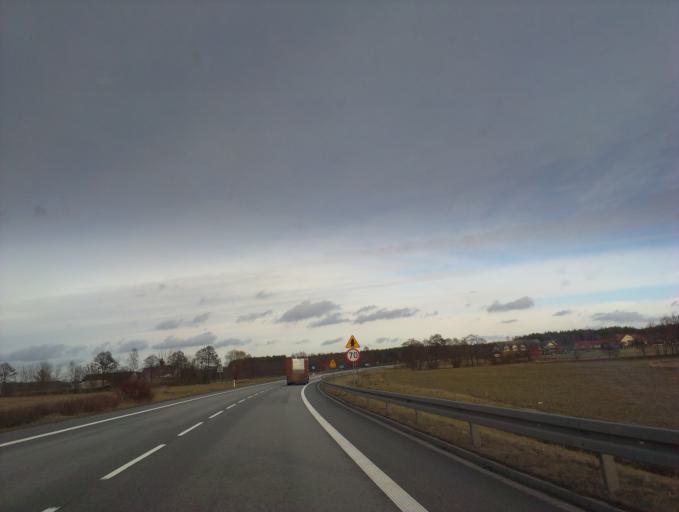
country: PL
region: Kujawsko-Pomorskie
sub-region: Powiat lipnowski
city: Skepe
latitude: 52.8753
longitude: 19.3204
